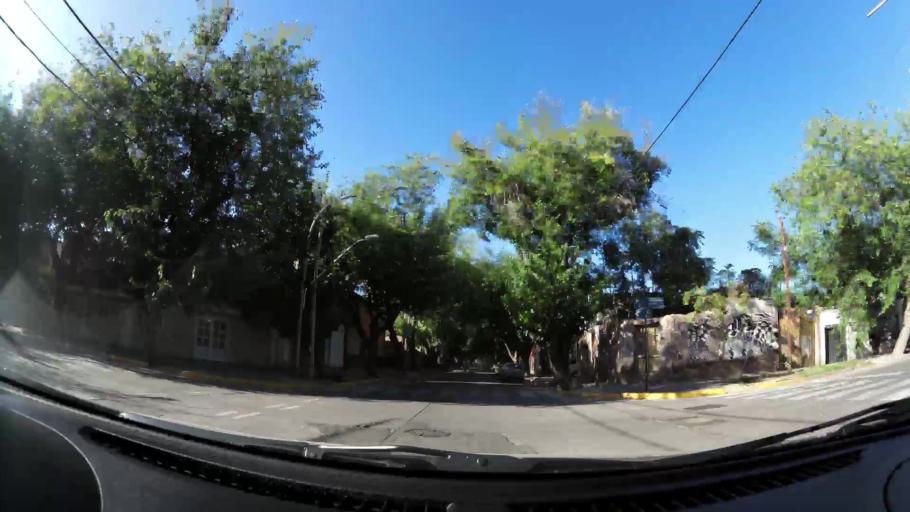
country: AR
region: Mendoza
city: Las Heras
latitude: -32.8678
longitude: -68.8256
